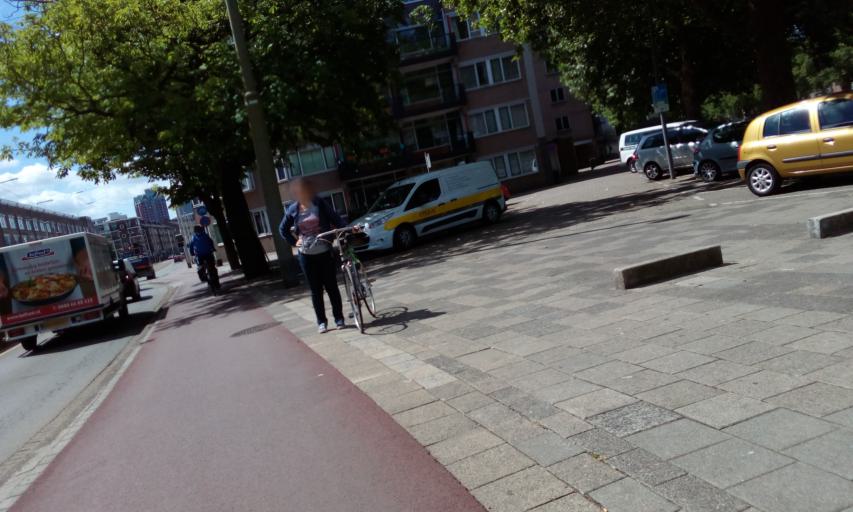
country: NL
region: South Holland
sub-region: Gemeente Rotterdam
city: Rotterdam
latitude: 51.9295
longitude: 4.4863
